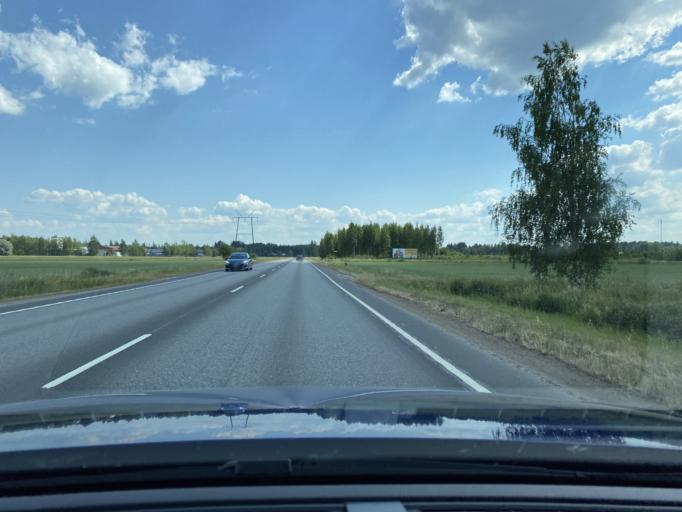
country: FI
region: Satakunta
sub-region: Rauma
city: Eura
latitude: 61.1425
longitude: 22.1107
